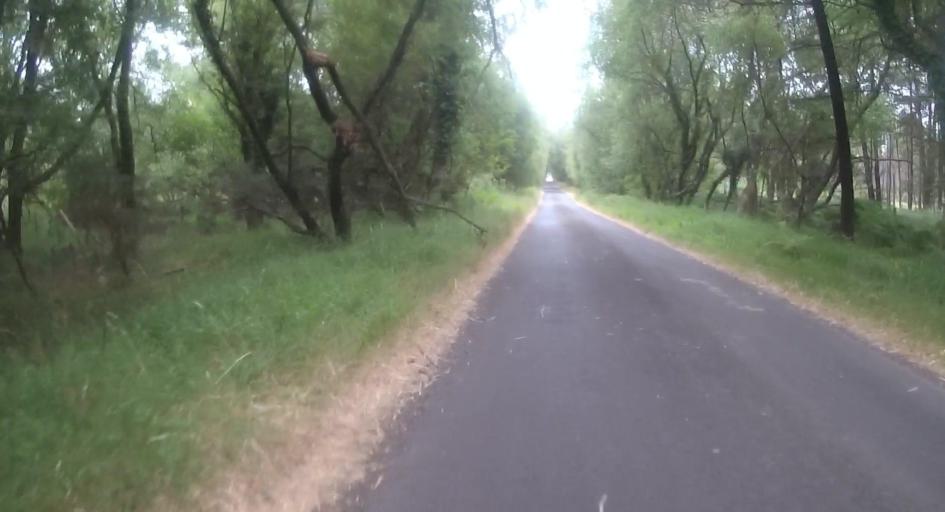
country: GB
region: England
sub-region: Dorset
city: Bovington Camp
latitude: 50.7281
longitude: -2.2514
